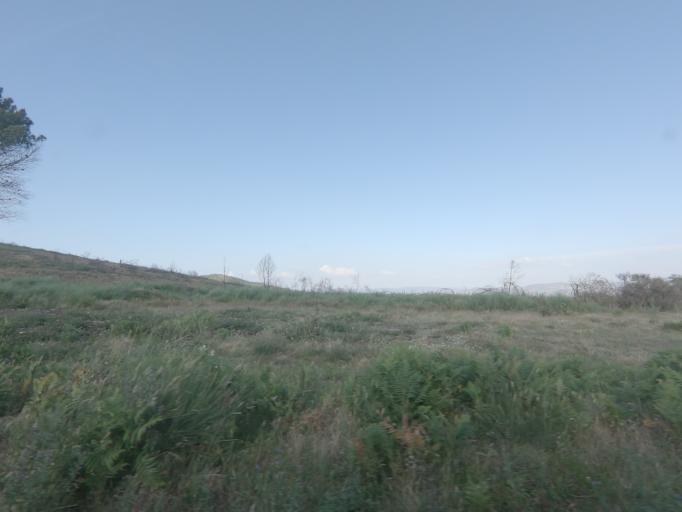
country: PT
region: Vila Real
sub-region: Sabrosa
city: Vilela
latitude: 41.2170
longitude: -7.5999
